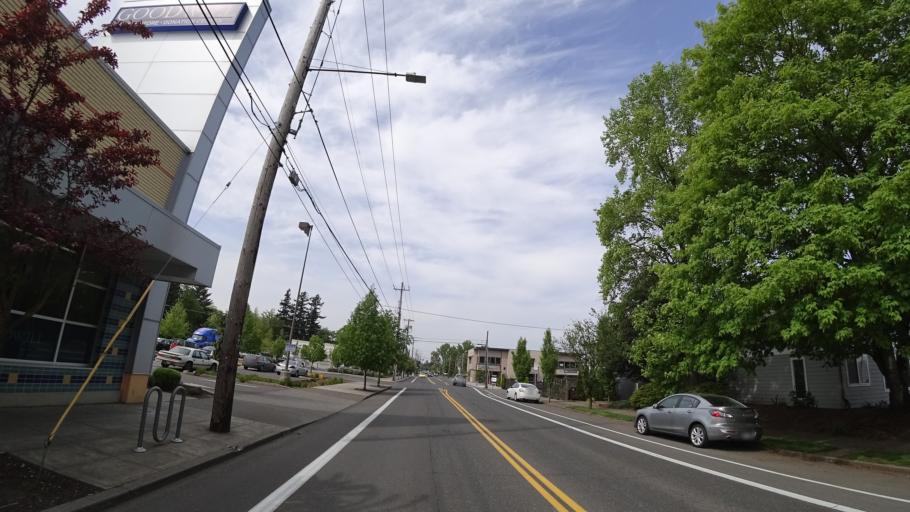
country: US
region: Oregon
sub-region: Multnomah County
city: Lents
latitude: 45.4780
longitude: -122.6088
